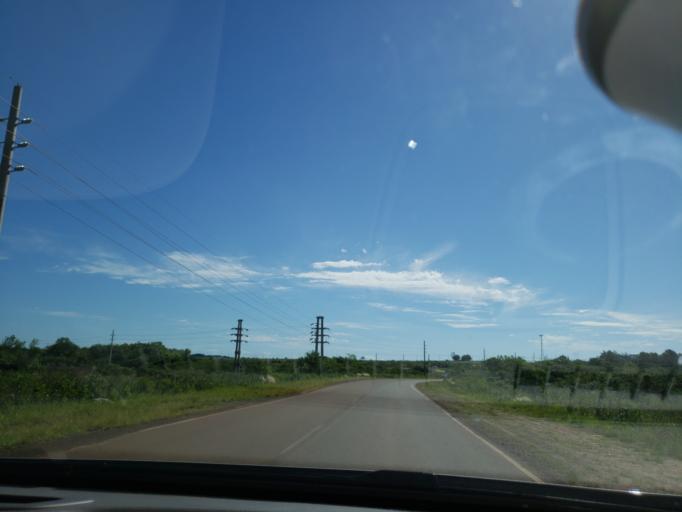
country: AR
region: Misiones
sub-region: Departamento de Capital
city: Posadas
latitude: -27.3901
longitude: -55.9840
